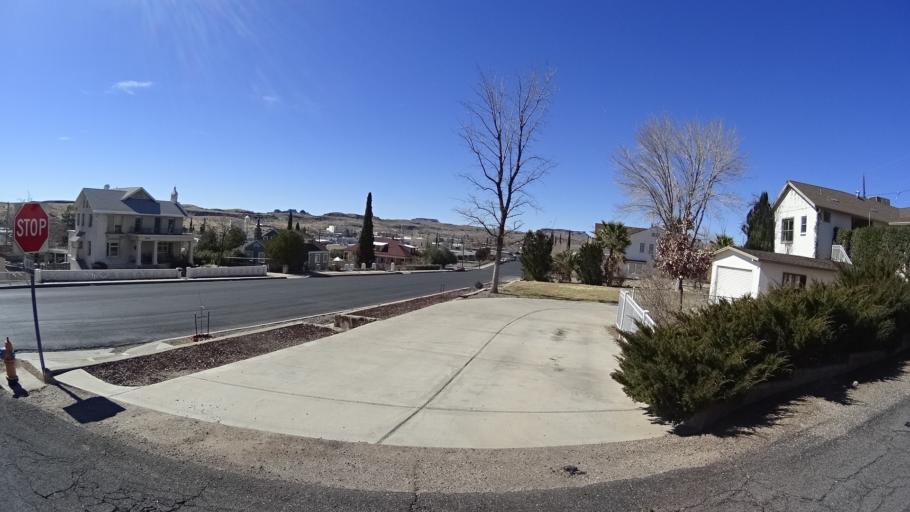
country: US
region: Arizona
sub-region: Mohave County
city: Kingman
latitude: 35.1900
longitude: -114.0475
